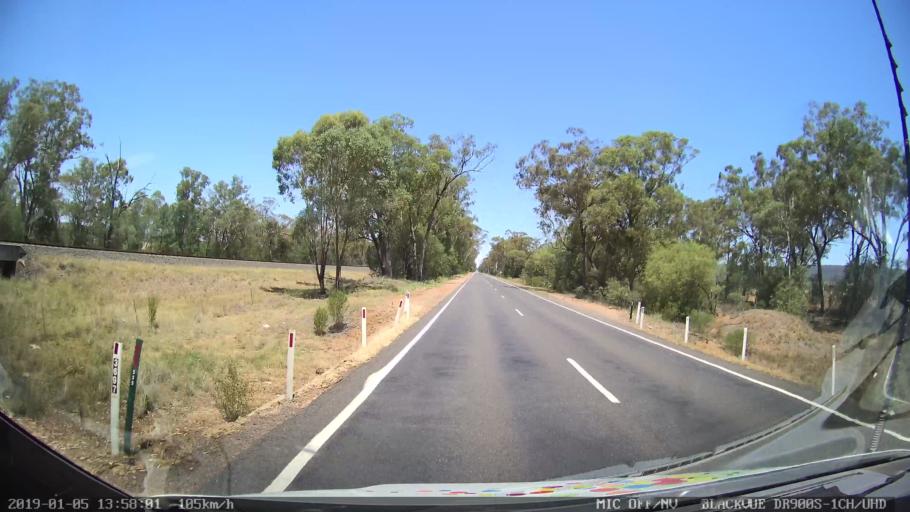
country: AU
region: New South Wales
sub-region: Gunnedah
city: Gunnedah
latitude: -31.1343
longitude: 150.2796
